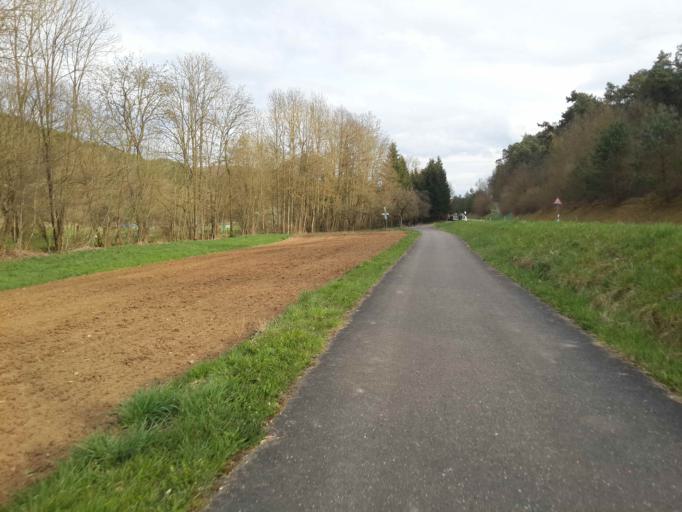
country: DE
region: Baden-Wuerttemberg
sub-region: Regierungsbezirk Stuttgart
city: Boxberg
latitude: 49.4974
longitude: 9.6010
